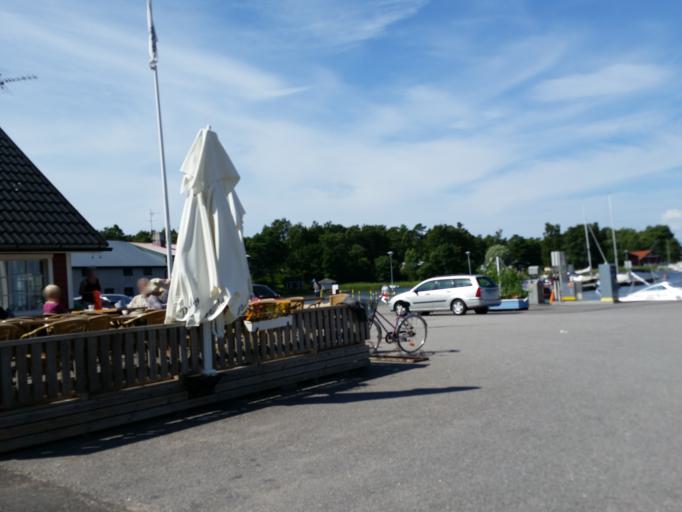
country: FI
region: Uusimaa
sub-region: Raaseporin
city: Hanko
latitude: 59.8421
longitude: 22.9480
